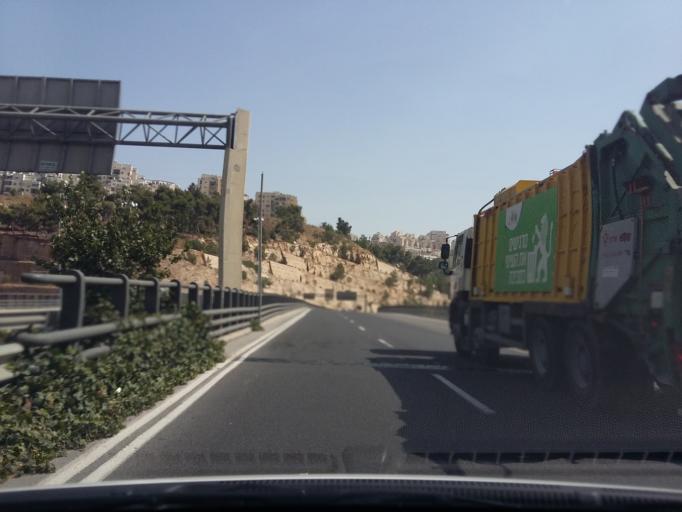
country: IL
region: Jerusalem
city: West Jerusalem
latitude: 31.8027
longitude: 35.2041
